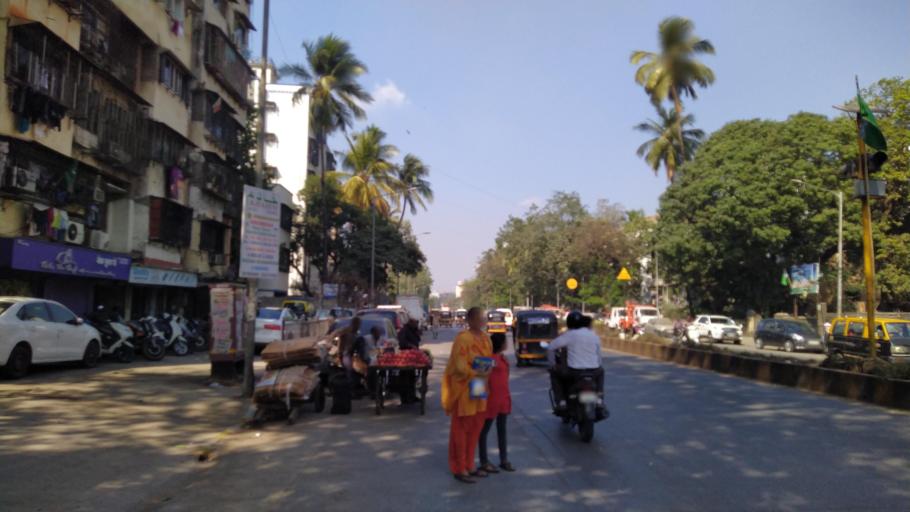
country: IN
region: Maharashtra
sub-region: Mumbai Suburban
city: Mumbai
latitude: 19.0681
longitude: 72.8750
